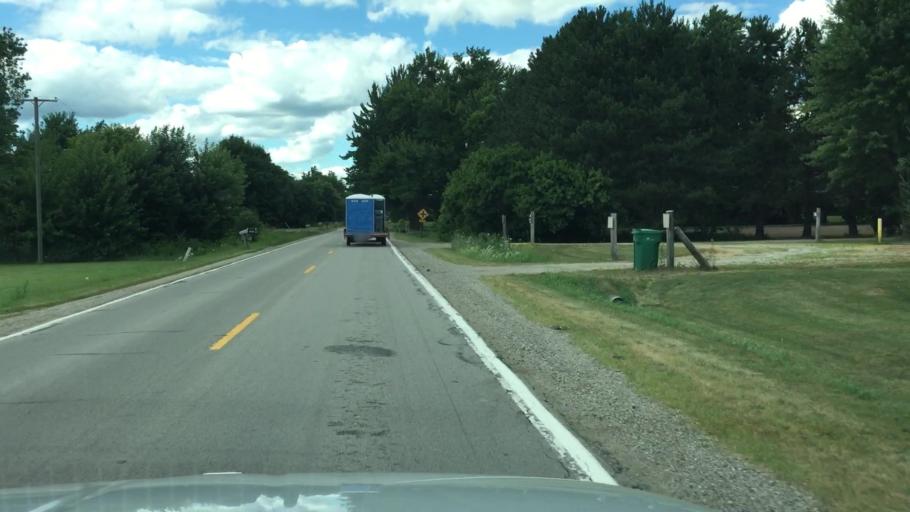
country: US
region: Michigan
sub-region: Macomb County
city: Armada
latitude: 42.9057
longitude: -82.9453
